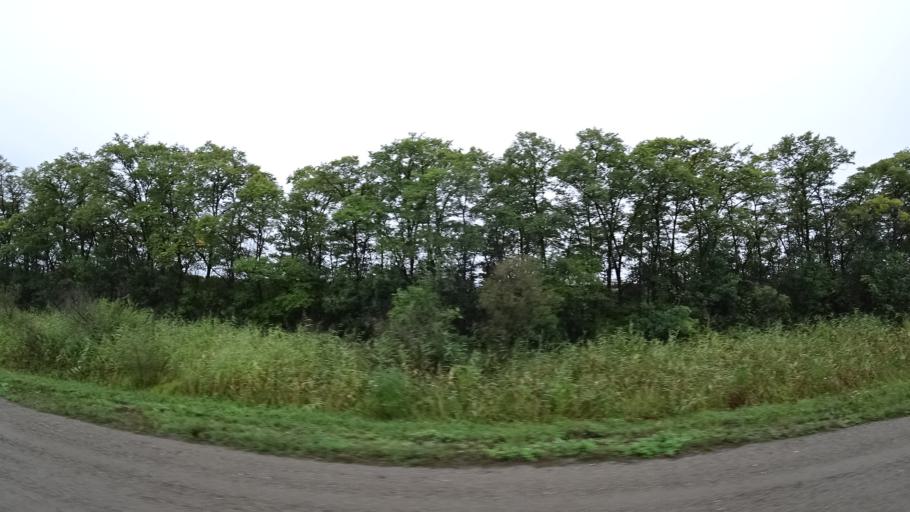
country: RU
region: Primorskiy
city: Monastyrishche
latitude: 44.2226
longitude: 132.4522
